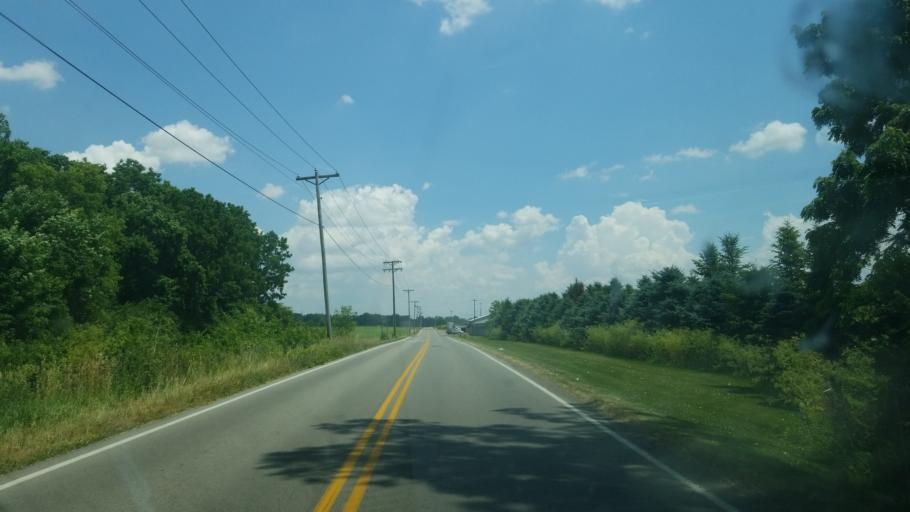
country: US
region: Ohio
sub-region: Hardin County
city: Kenton
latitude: 40.6328
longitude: -83.5908
